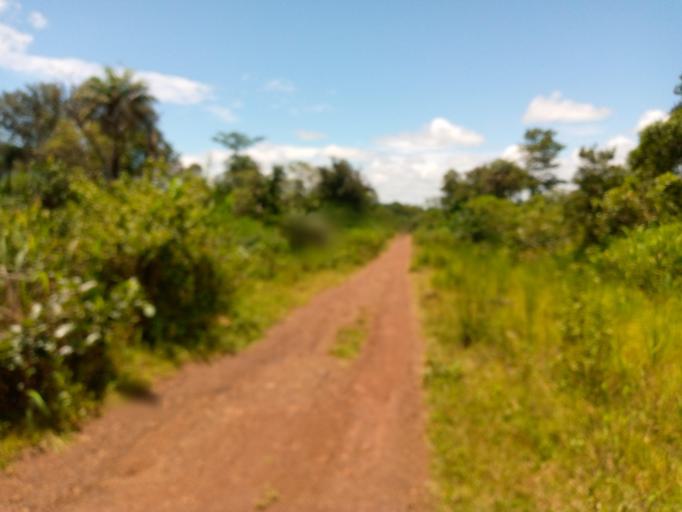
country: SL
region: Northern Province
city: Binkolo
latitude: 9.1149
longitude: -12.1355
